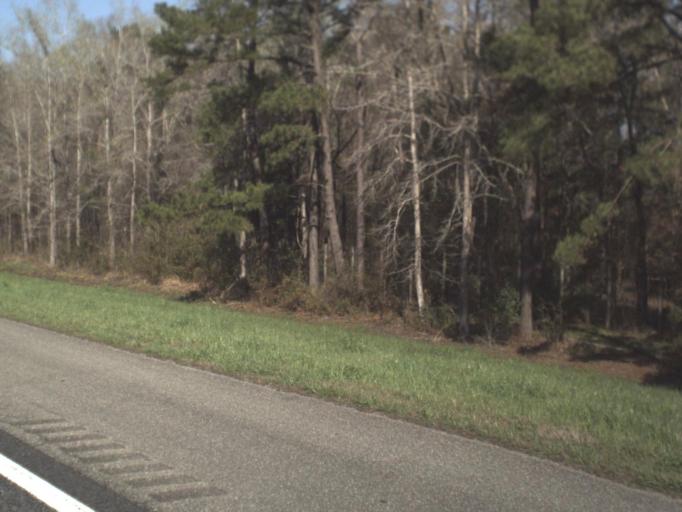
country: US
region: Florida
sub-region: Leon County
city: Tallahassee
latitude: 30.4783
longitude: -84.0997
